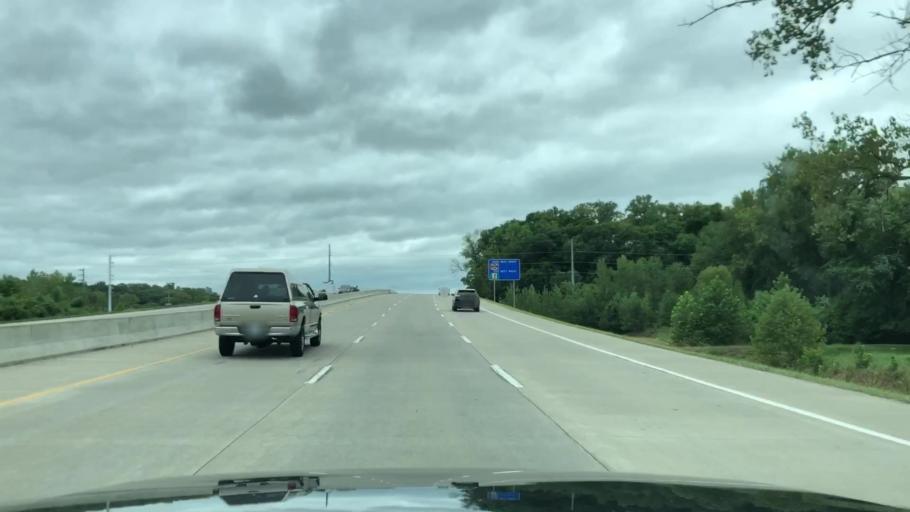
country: US
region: Missouri
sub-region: Saint Louis County
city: Maryland Heights
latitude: 38.6945
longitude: -90.5013
